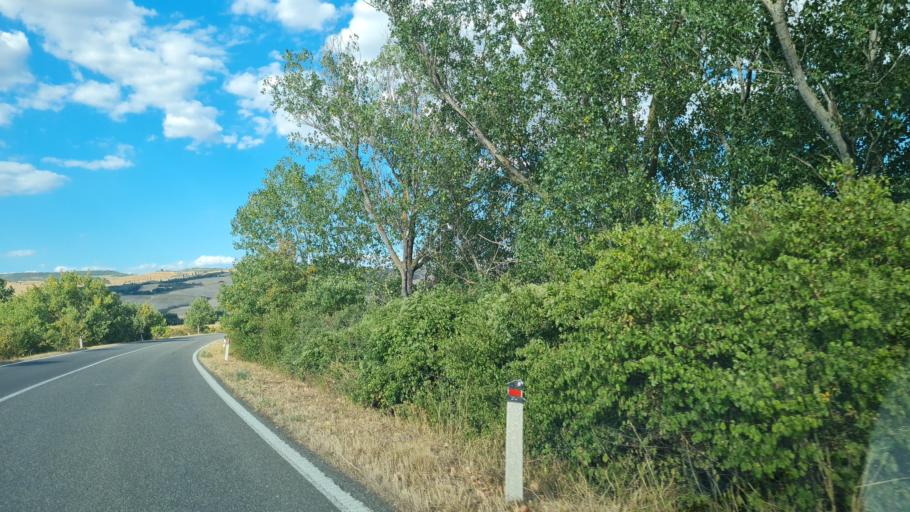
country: IT
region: Tuscany
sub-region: Provincia di Siena
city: Chianciano Terme
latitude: 43.0057
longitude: 11.7308
